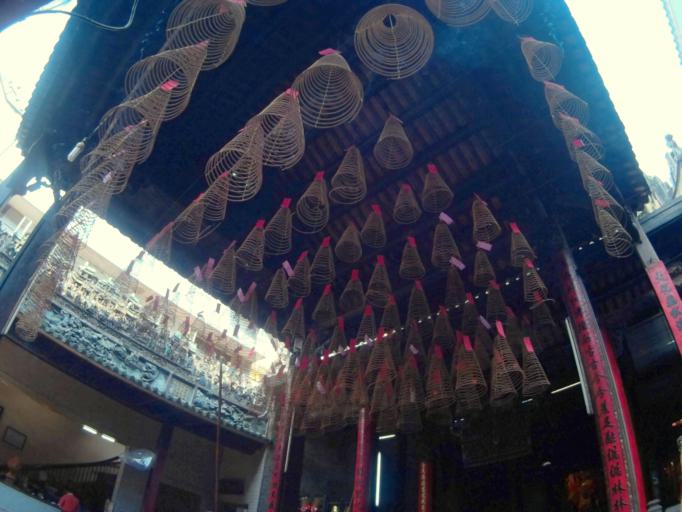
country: VN
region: Ho Chi Minh City
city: Quan Nam
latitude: 10.7535
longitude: 106.6613
